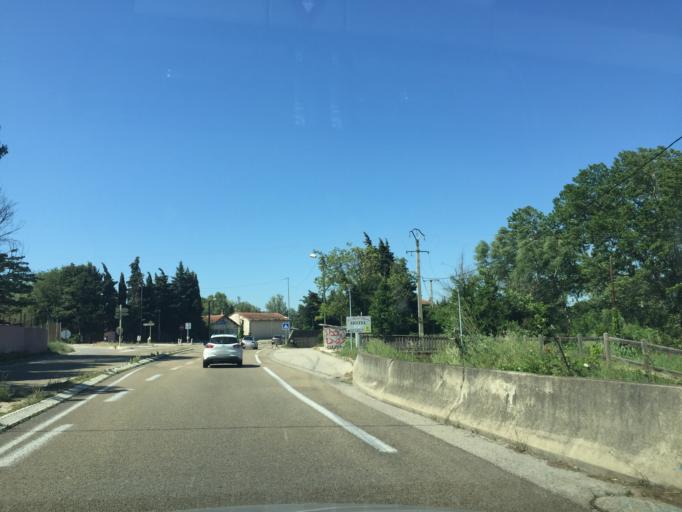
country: FR
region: Languedoc-Roussillon
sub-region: Departement du Gard
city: Saze
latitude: 43.9516
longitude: 4.7117
